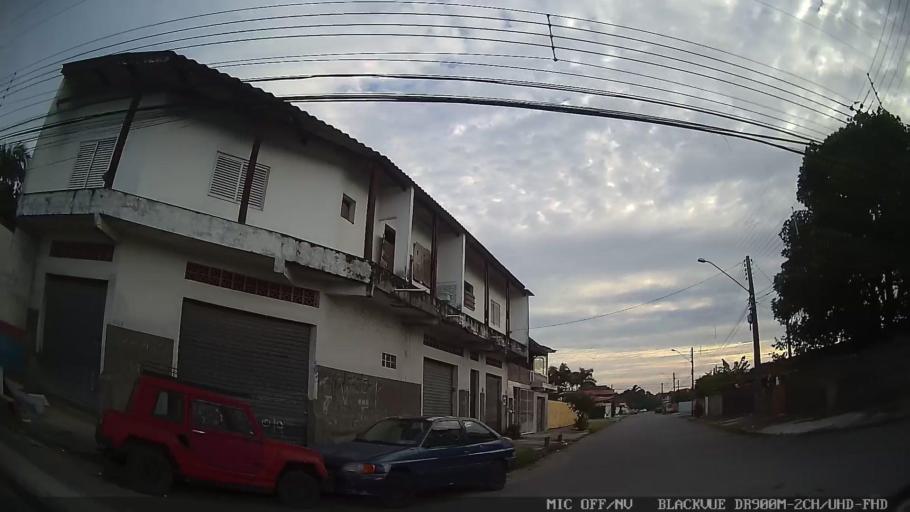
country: BR
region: Sao Paulo
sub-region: Itanhaem
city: Itanhaem
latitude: -24.1682
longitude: -46.7744
